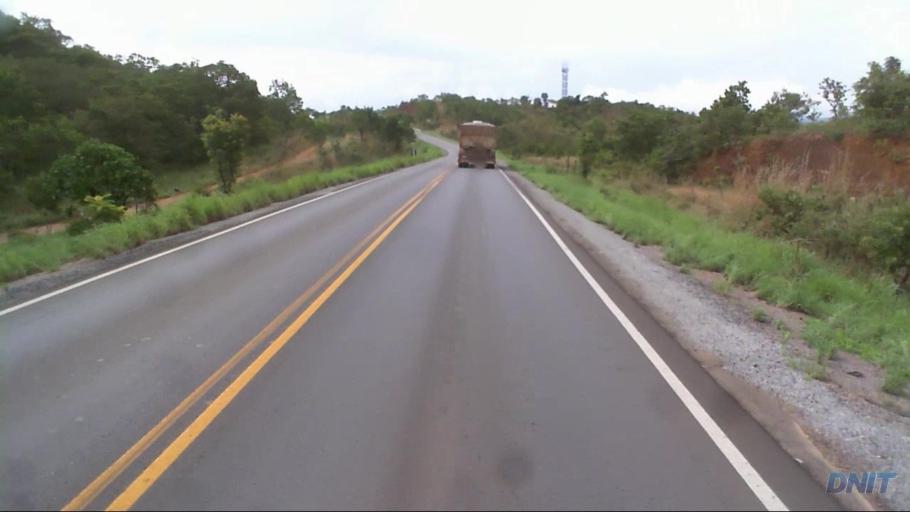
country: BR
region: Goias
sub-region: Padre Bernardo
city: Padre Bernardo
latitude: -15.2198
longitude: -48.2803
